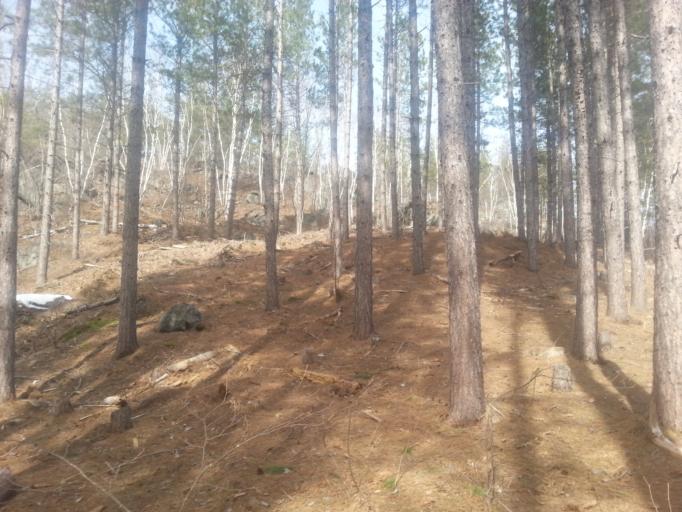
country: CA
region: Ontario
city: Greater Sudbury
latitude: 46.5429
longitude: -80.6450
